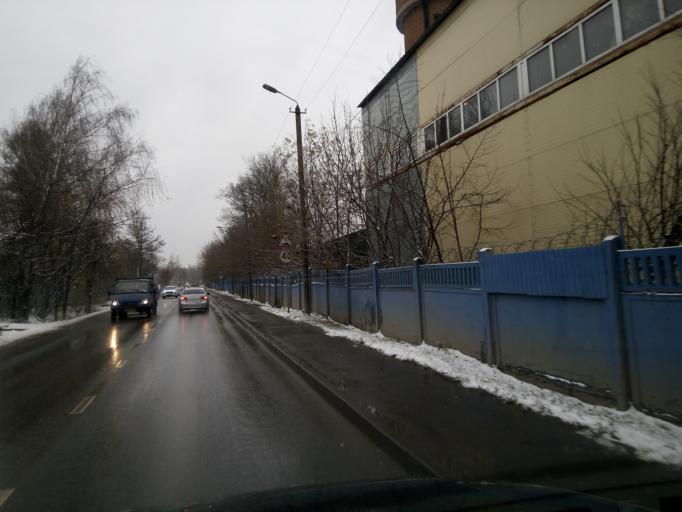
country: RU
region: Moskovskaya
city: Skhodnya
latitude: 55.9433
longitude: 37.2807
